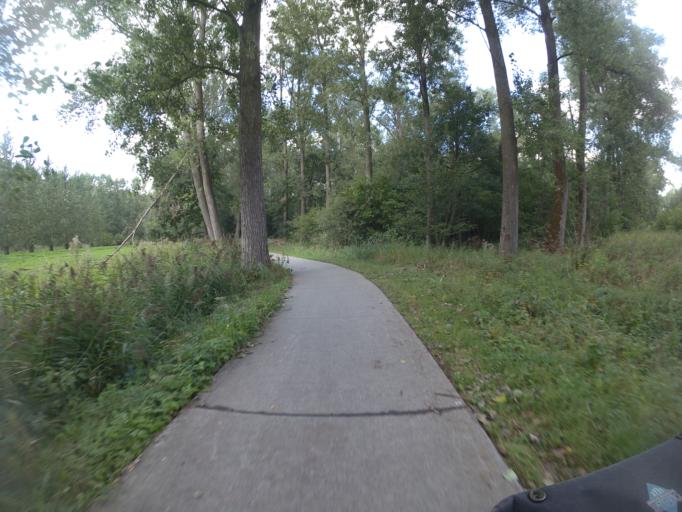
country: NL
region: North Brabant
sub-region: Gemeente Schijndel
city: Schijndel
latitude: 51.6343
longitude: 5.4662
